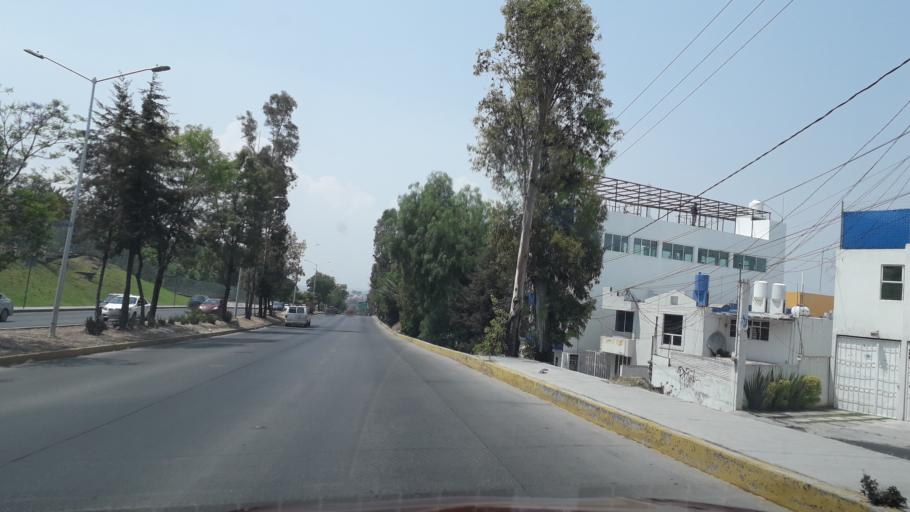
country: MX
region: Puebla
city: Puebla
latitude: 19.0590
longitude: -98.1882
